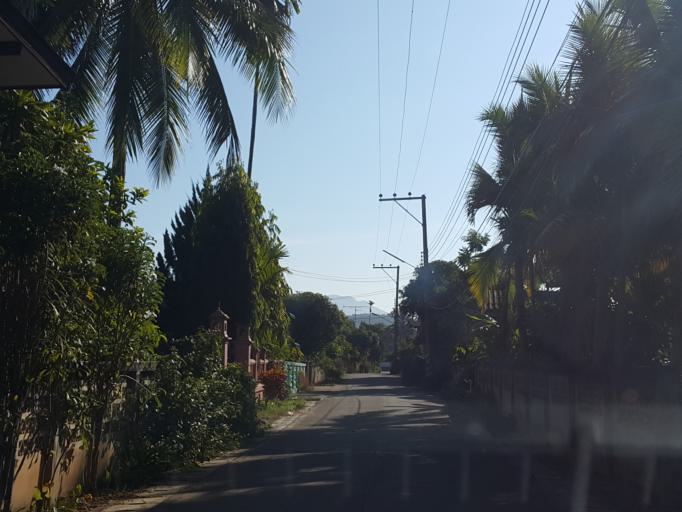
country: TH
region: Chiang Mai
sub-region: Amphoe Chiang Dao
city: Chiang Dao
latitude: 19.4670
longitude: 98.9632
